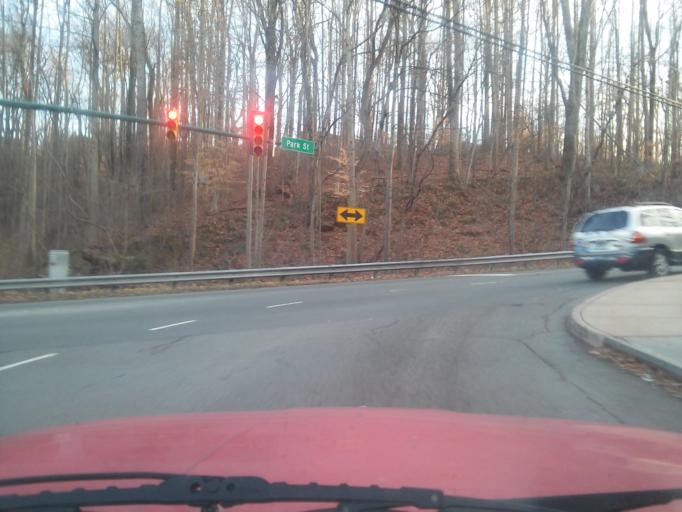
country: US
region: Virginia
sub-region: City of Charlottesville
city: Charlottesville
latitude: 38.0472
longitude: -78.4701
